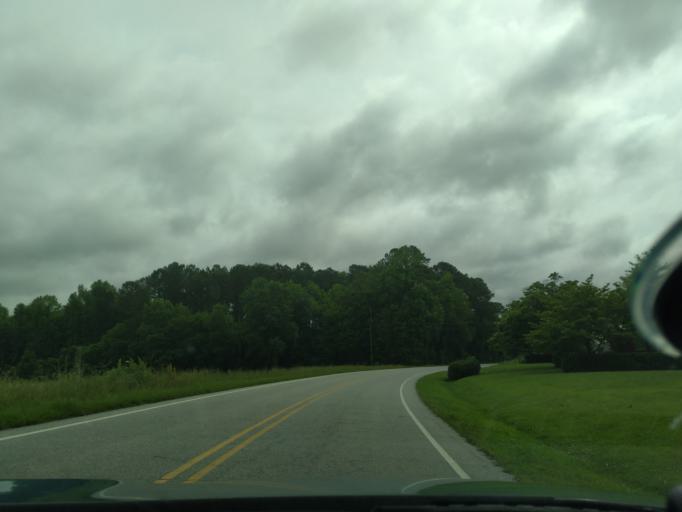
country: US
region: North Carolina
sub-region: Washington County
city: Plymouth
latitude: 35.8535
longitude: -76.7302
